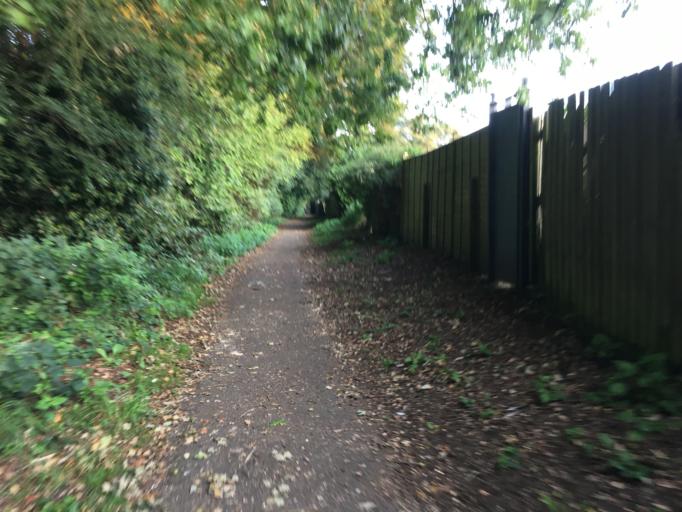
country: GB
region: England
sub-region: Warwickshire
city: Rugby
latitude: 52.3581
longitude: -1.2666
